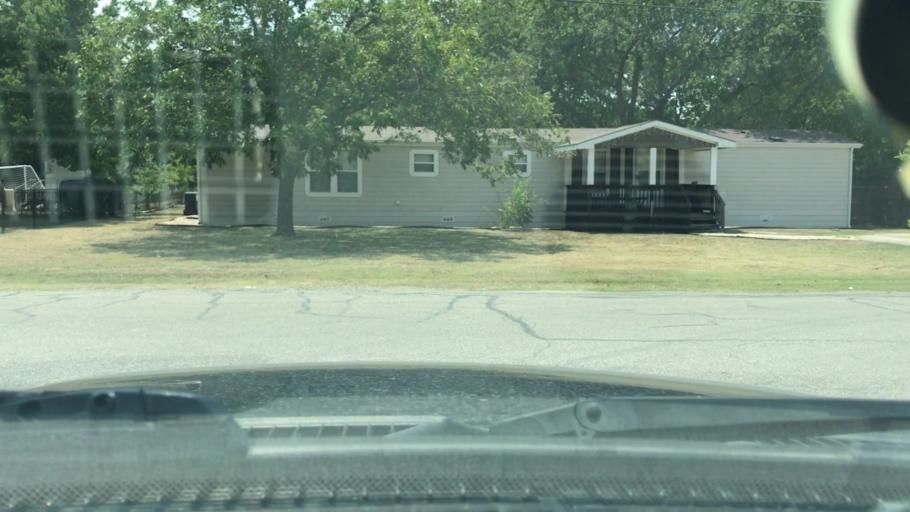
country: US
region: Texas
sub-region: Williamson County
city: Cedar Park
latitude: 30.5348
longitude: -97.8403
